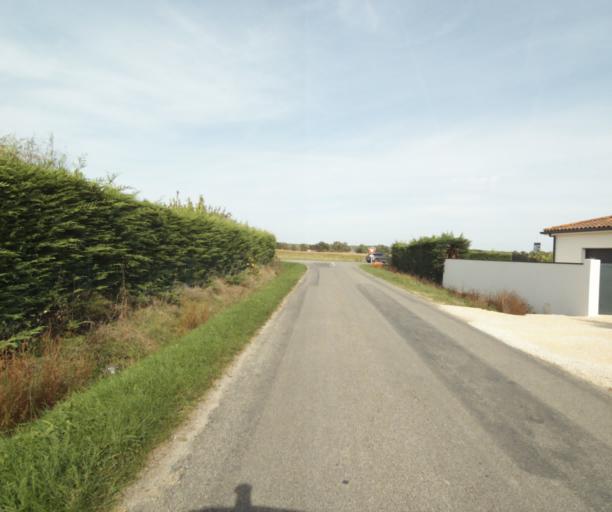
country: FR
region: Midi-Pyrenees
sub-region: Departement du Tarn-et-Garonne
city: Labastide-Saint-Pierre
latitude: 43.9127
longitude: 1.3809
